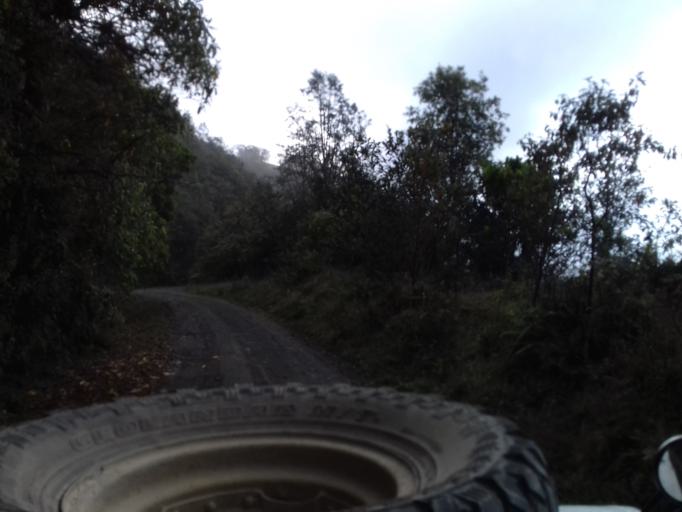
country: CO
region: Quindio
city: Salento
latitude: 4.5549
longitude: -75.5042
